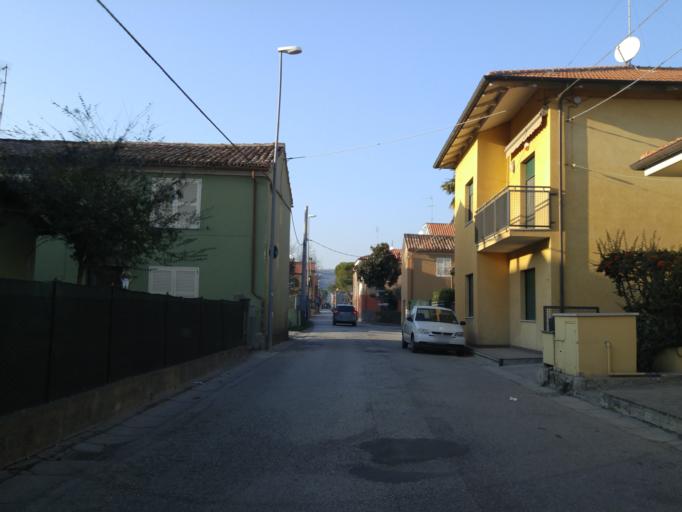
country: IT
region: The Marches
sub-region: Provincia di Pesaro e Urbino
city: Bellocchi
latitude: 43.7982
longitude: 12.9963
